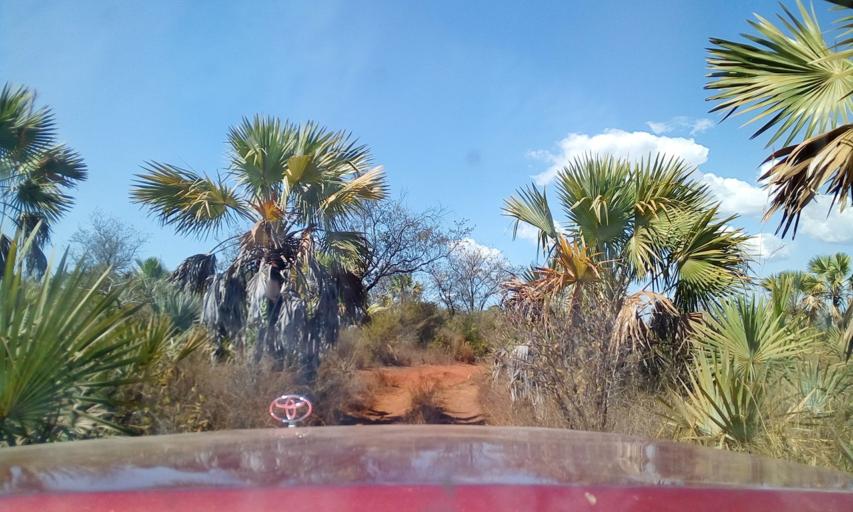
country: MG
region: Boeny
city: Sitampiky
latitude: -16.1259
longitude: 45.4394
